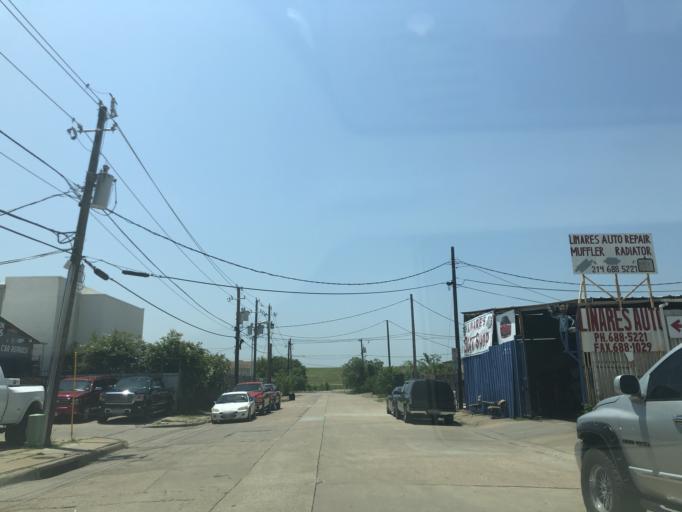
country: US
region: Texas
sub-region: Dallas County
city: Dallas
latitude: 32.8040
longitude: -96.8512
